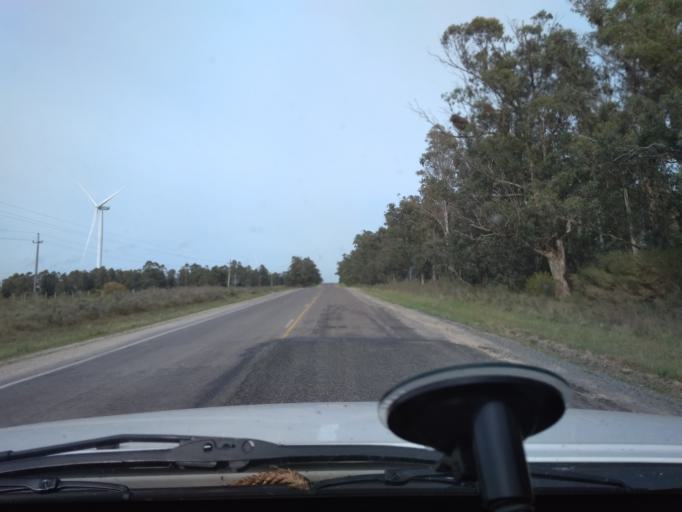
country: UY
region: Florida
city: Florida
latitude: -34.0857
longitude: -56.0916
